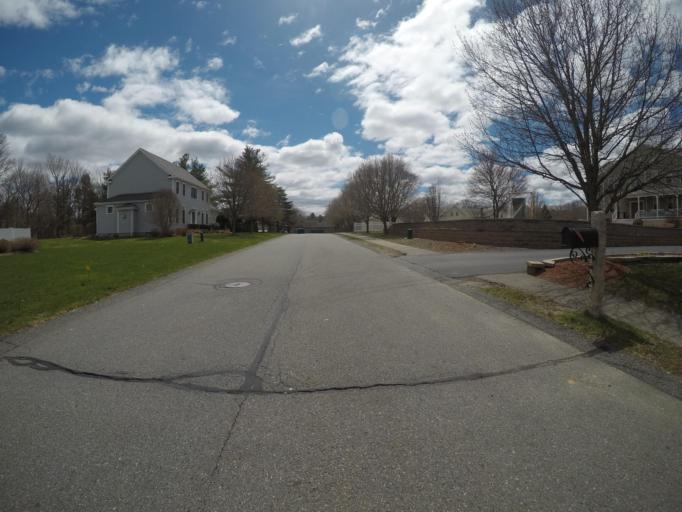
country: US
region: Massachusetts
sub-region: Norfolk County
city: Stoughton
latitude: 42.0773
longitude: -71.0820
